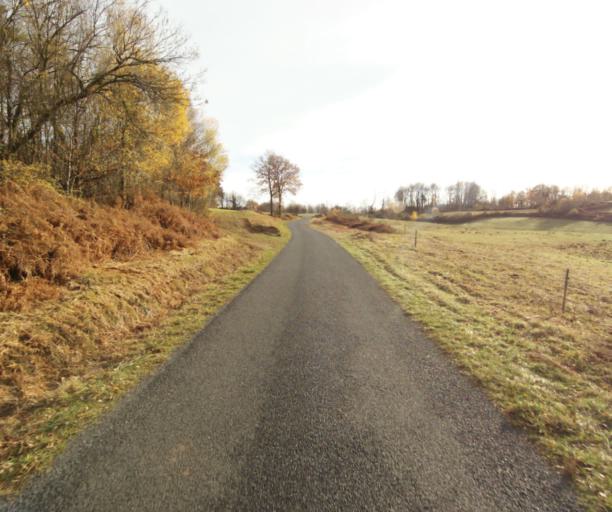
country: FR
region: Limousin
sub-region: Departement de la Correze
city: Sainte-Fortunade
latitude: 45.1822
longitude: 1.7909
